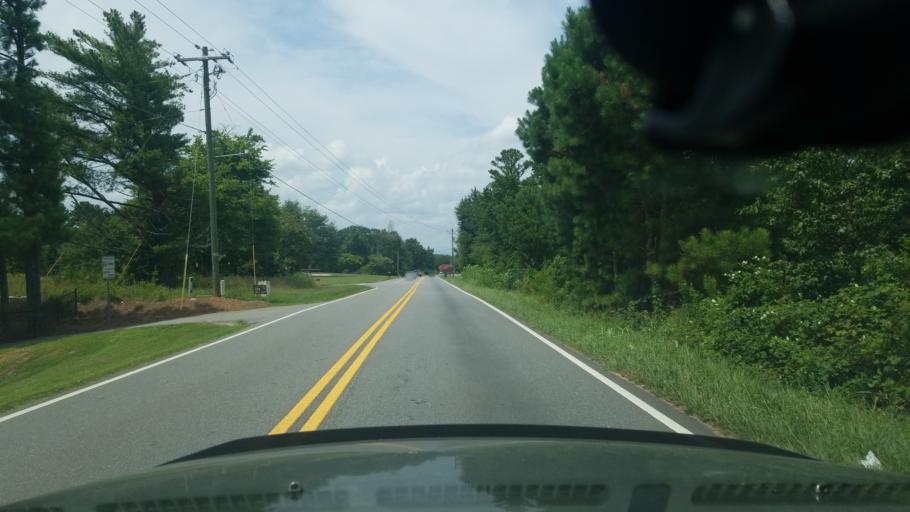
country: US
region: Georgia
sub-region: Forsyth County
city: Cumming
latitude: 34.2541
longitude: -84.2386
